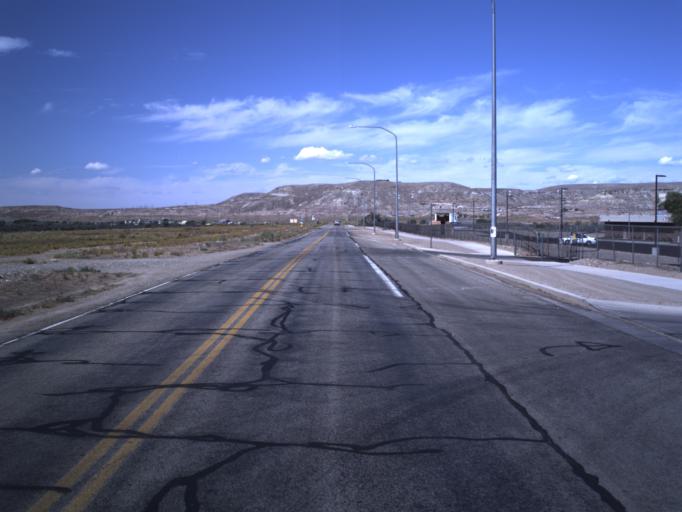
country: US
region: Utah
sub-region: San Juan County
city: Blanding
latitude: 37.2653
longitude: -109.3117
